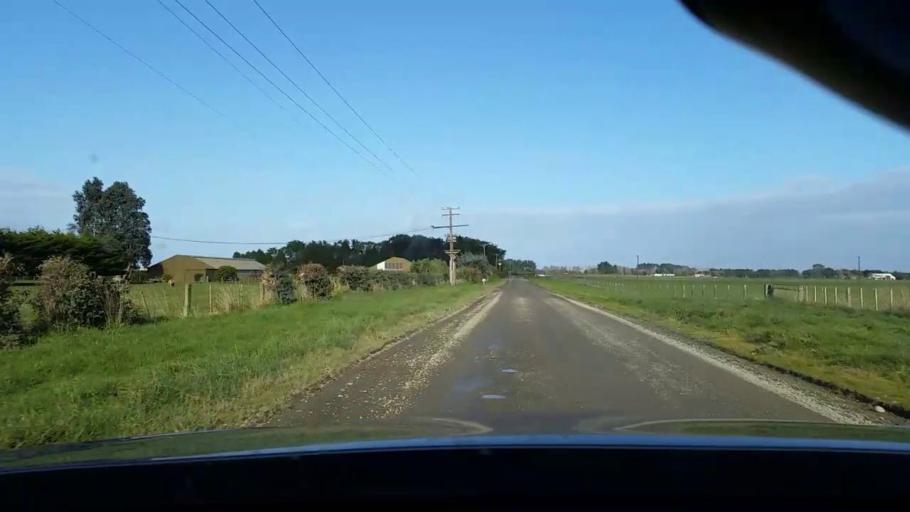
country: NZ
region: Southland
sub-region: Invercargill City
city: Invercargill
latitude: -46.3057
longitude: 168.3034
